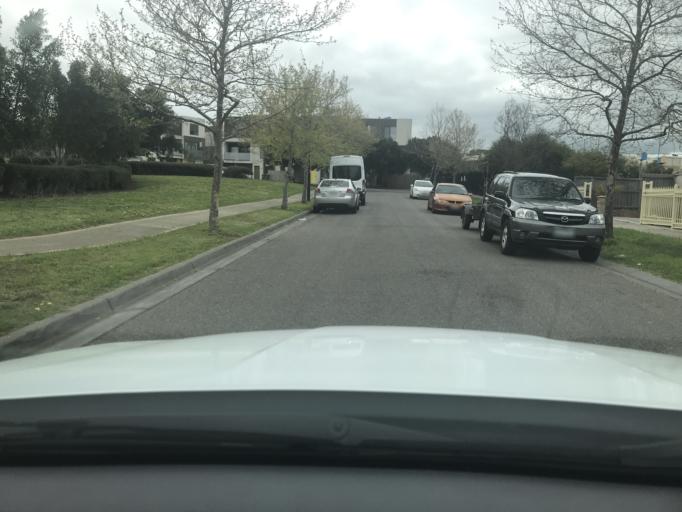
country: AU
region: Victoria
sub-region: Hume
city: Craigieburn
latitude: -37.5770
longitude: 144.9324
